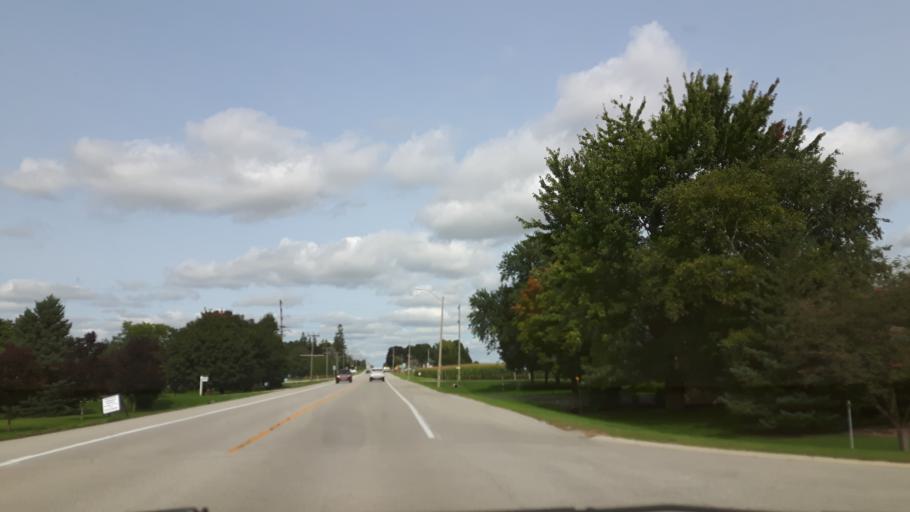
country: CA
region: Ontario
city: Huron East
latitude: 43.5602
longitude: -81.3876
